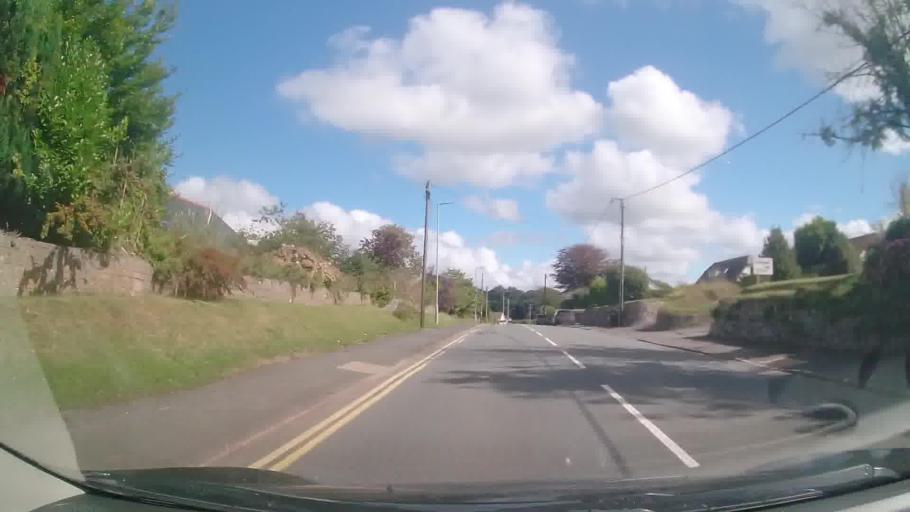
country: GB
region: Wales
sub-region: Pembrokeshire
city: Pembroke
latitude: 51.6754
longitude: -4.9054
